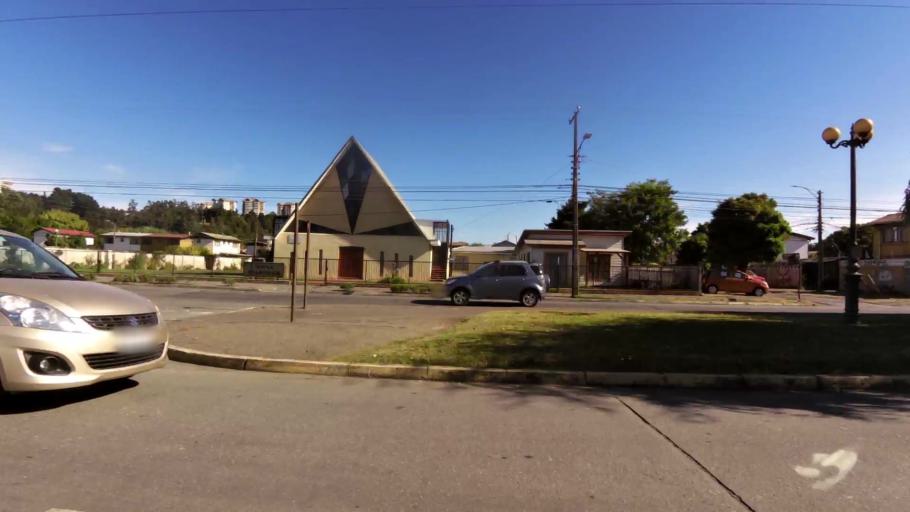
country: CL
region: Biobio
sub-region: Provincia de Concepcion
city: Concepcion
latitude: -36.8439
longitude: -73.1019
